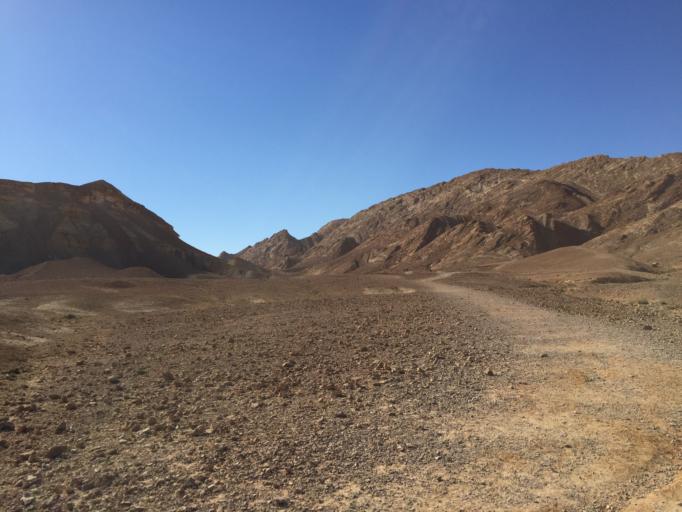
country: IL
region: Southern District
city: Mitzpe Ramon
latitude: 30.5769
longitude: 34.8824
